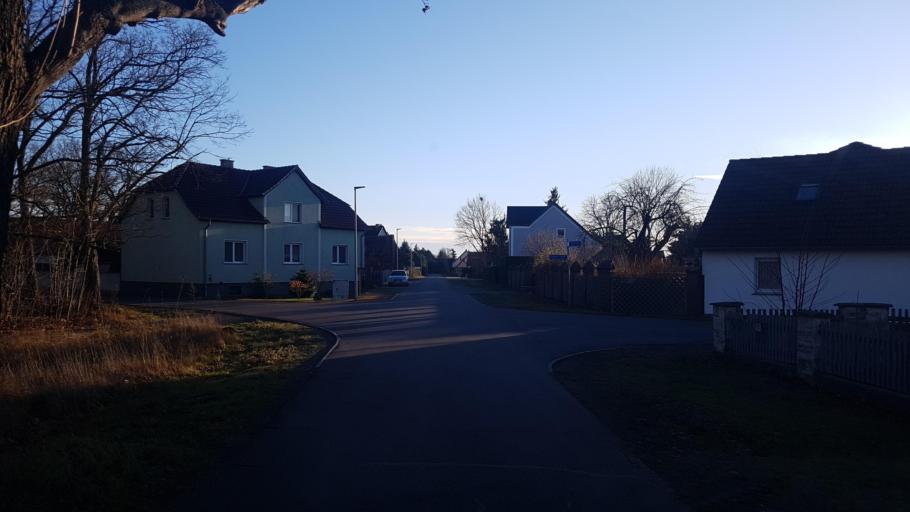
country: DE
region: Brandenburg
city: Peitz
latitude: 51.8857
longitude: 14.4182
